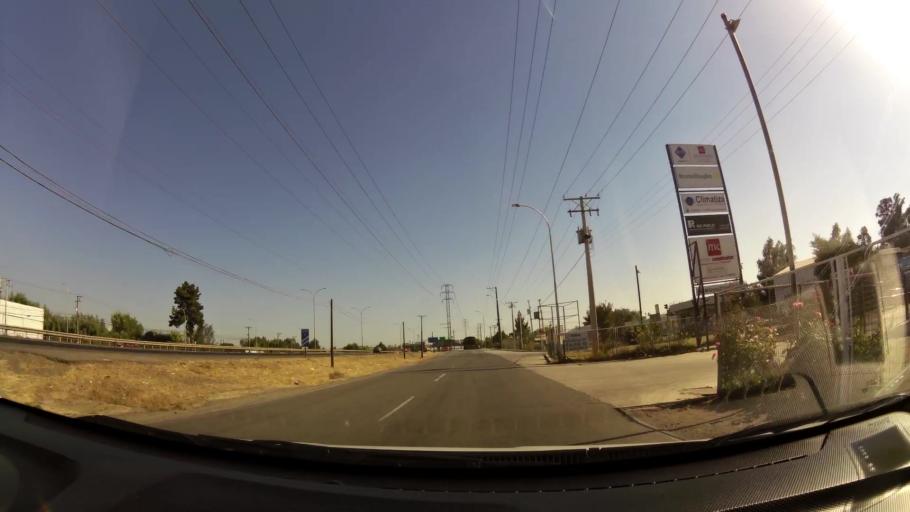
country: CL
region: Maule
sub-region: Provincia de Talca
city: Talca
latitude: -35.4489
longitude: -71.6443
